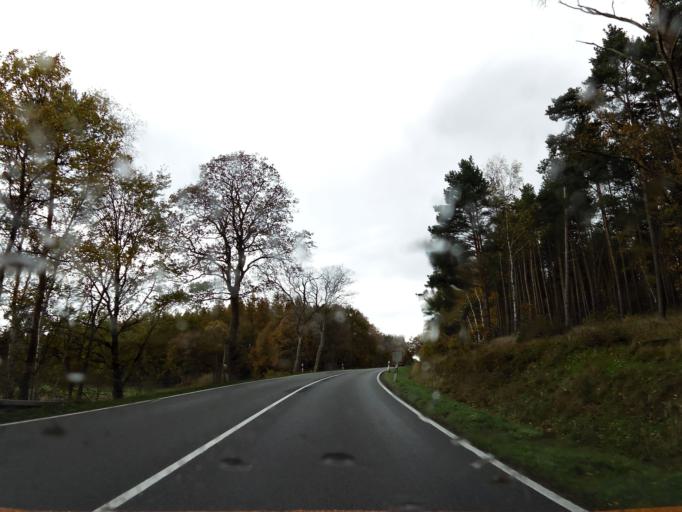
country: DE
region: Saxony-Anhalt
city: Kalbe
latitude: 52.6289
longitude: 11.3090
